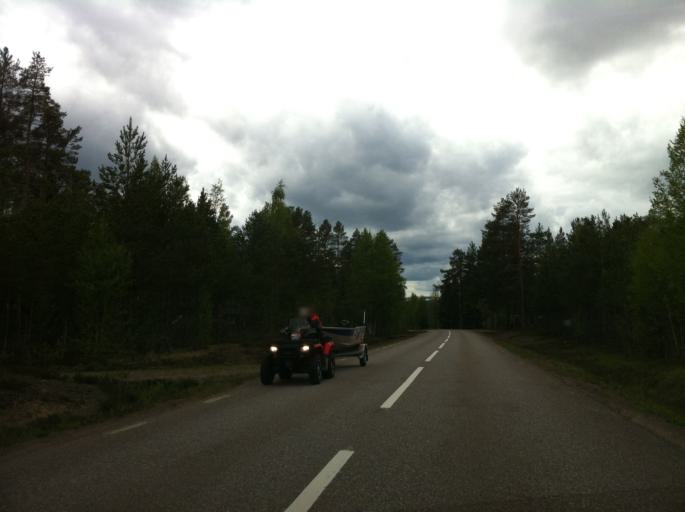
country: NO
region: Hedmark
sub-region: Trysil
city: Innbygda
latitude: 61.4368
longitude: 13.1012
